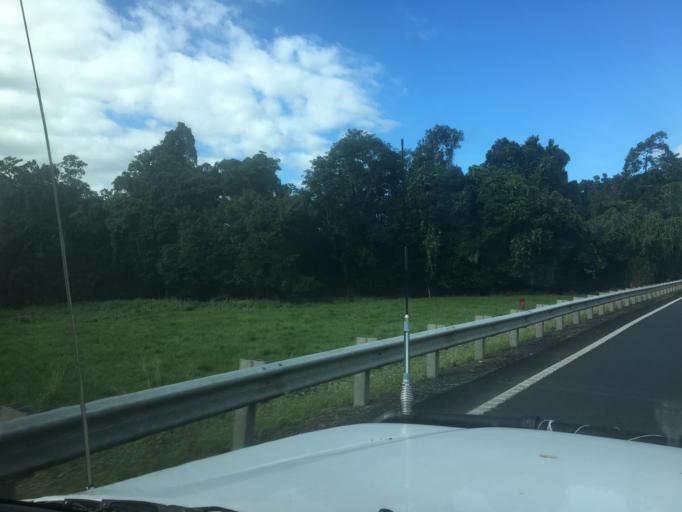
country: AU
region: Queensland
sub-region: Cassowary Coast
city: Innisfail
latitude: -17.2587
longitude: 145.9220
